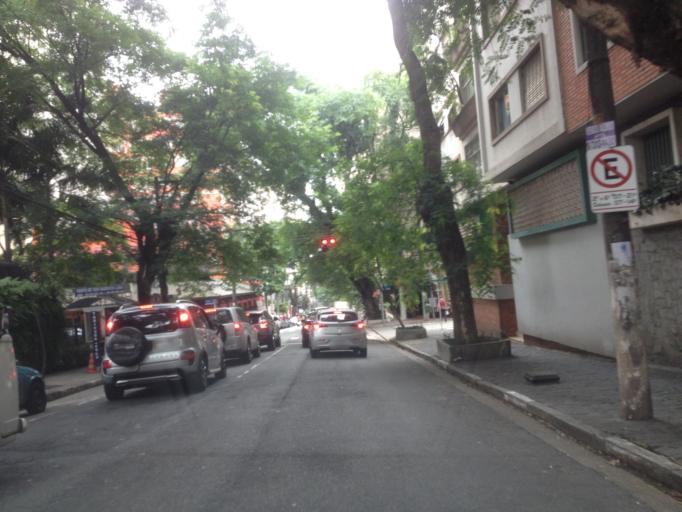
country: BR
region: Sao Paulo
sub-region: Sao Paulo
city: Sao Paulo
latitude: -23.5616
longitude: -46.6656
